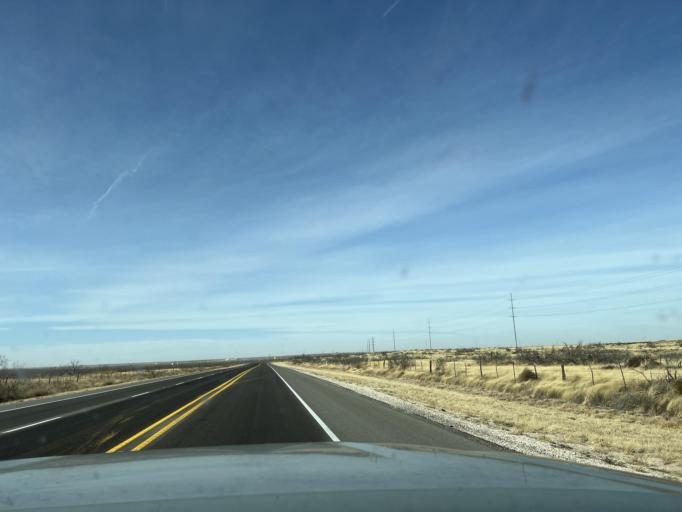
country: US
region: Texas
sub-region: Andrews County
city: Andrews
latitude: 32.3553
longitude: -102.7618
